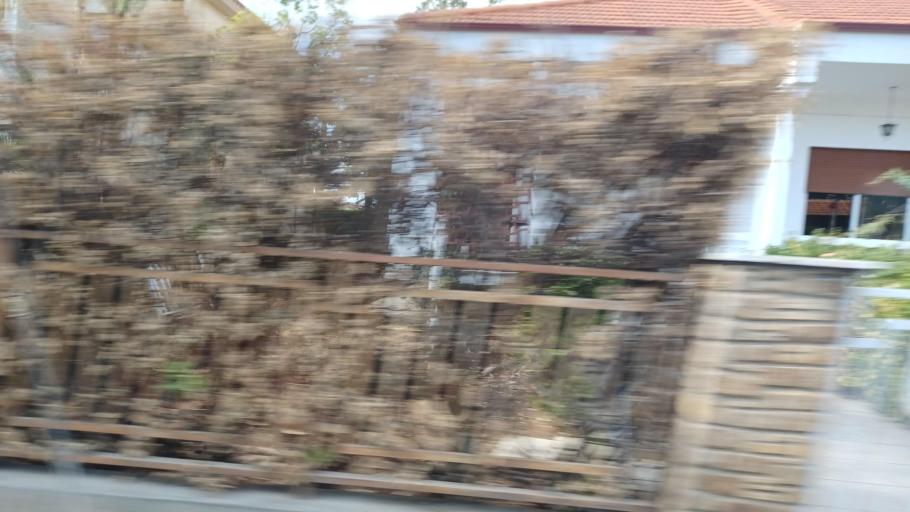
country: CY
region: Limassol
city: Pano Polemidia
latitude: 34.6949
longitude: 33.0002
